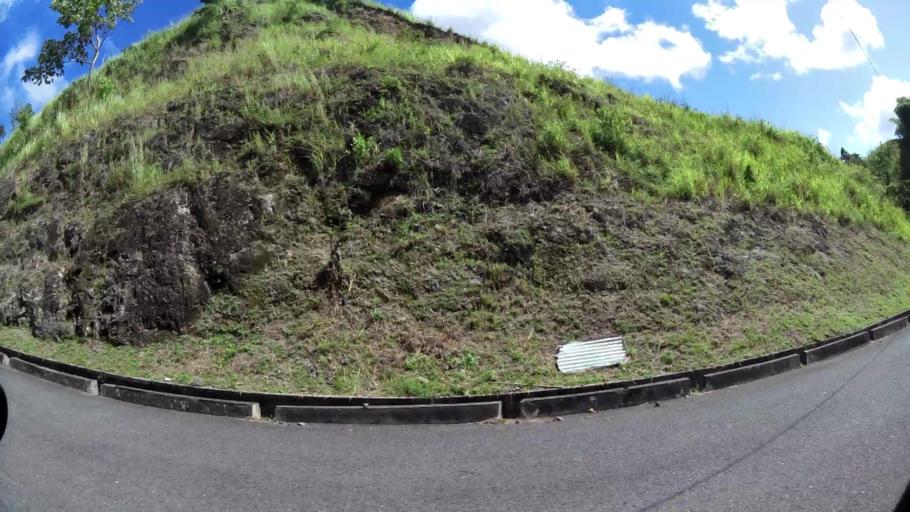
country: TT
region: Tobago
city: Scarborough
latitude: 11.2336
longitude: -60.7383
